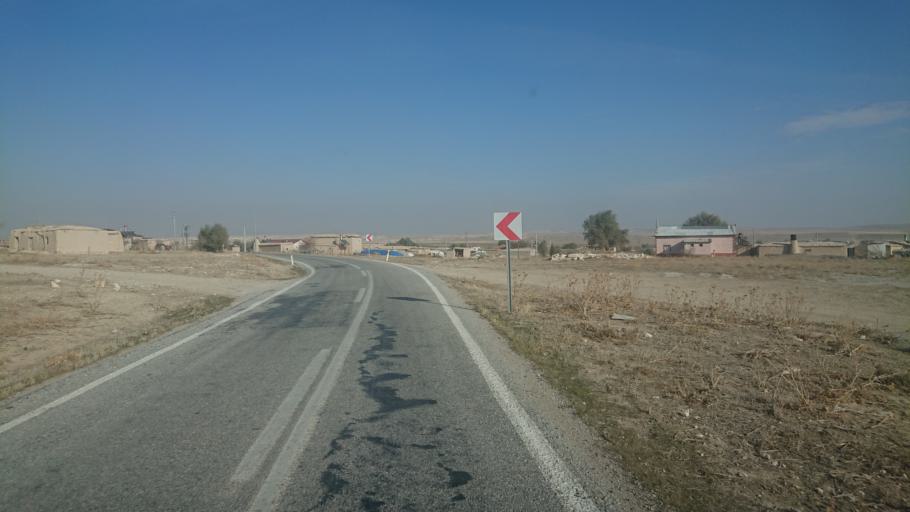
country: TR
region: Aksaray
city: Sultanhani
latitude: 38.0383
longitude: 33.5905
